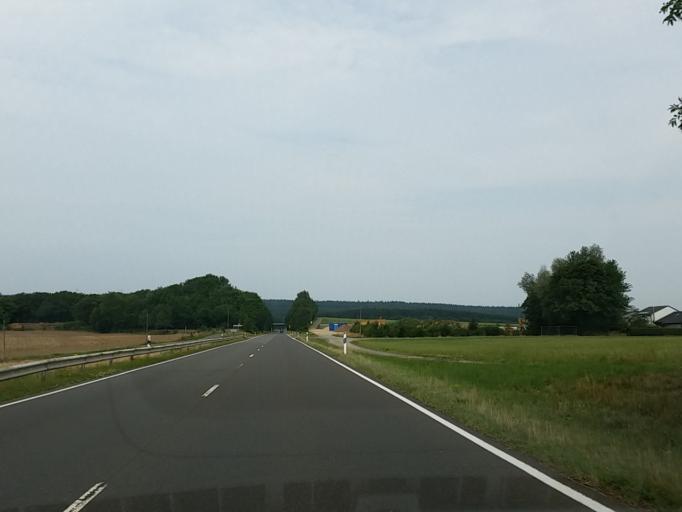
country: DE
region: Rheinland-Pfalz
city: Reinsfeld
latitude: 49.6852
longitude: 6.8925
